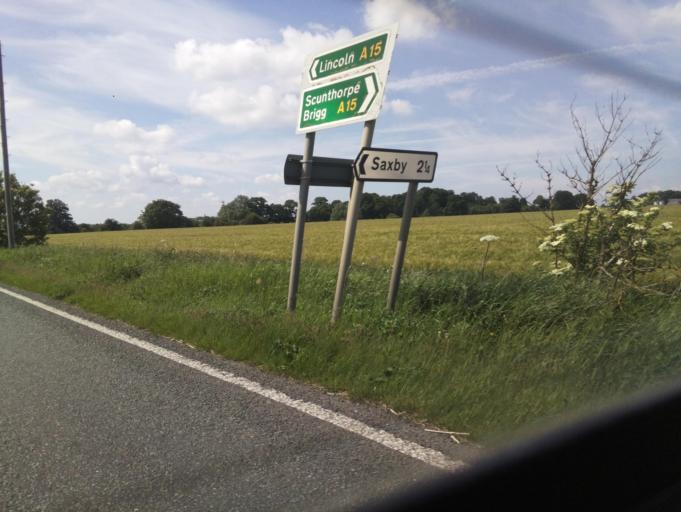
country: GB
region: England
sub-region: Lincolnshire
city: Burton
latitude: 53.3558
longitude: -0.5452
